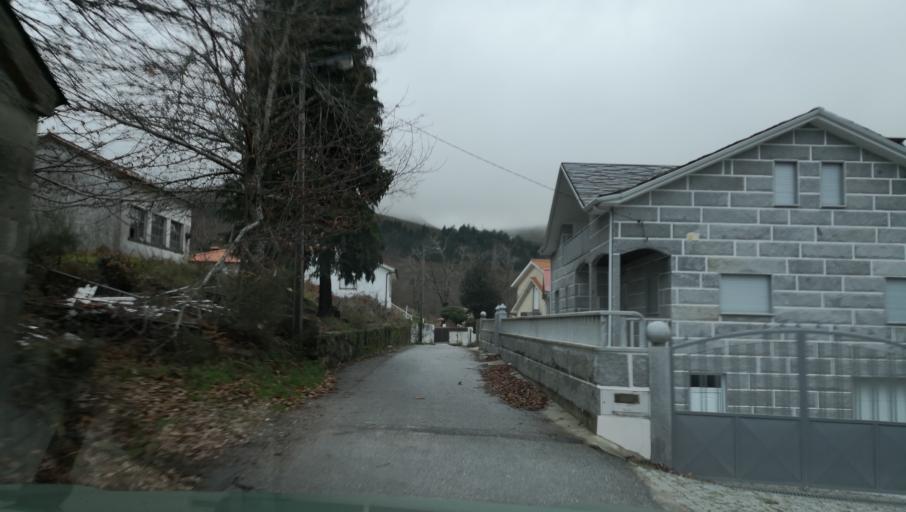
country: PT
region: Vila Real
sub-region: Mondim de Basto
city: Mondim de Basto
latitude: 41.3156
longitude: -7.8774
